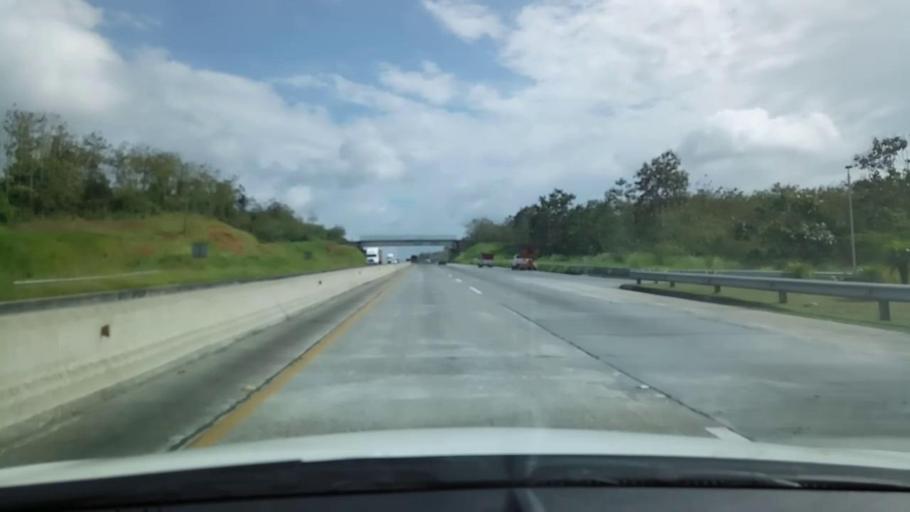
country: PA
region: Colon
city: El Giral
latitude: 9.2484
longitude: -79.6879
